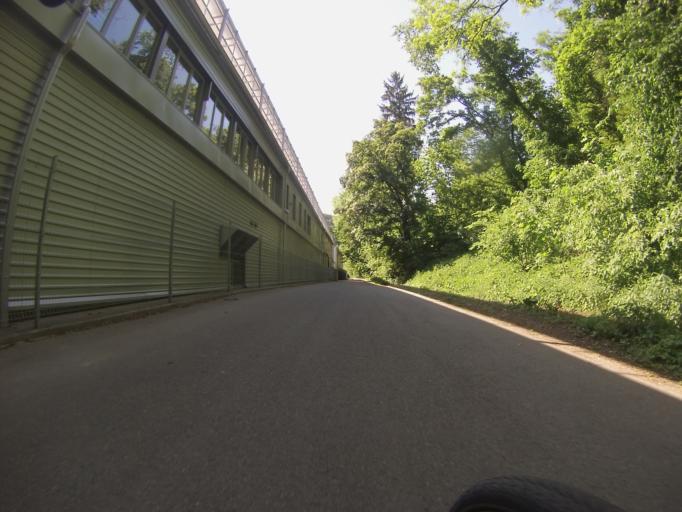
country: CZ
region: South Moravian
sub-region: Okres Blansko
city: Adamov
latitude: 49.3031
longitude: 16.6480
